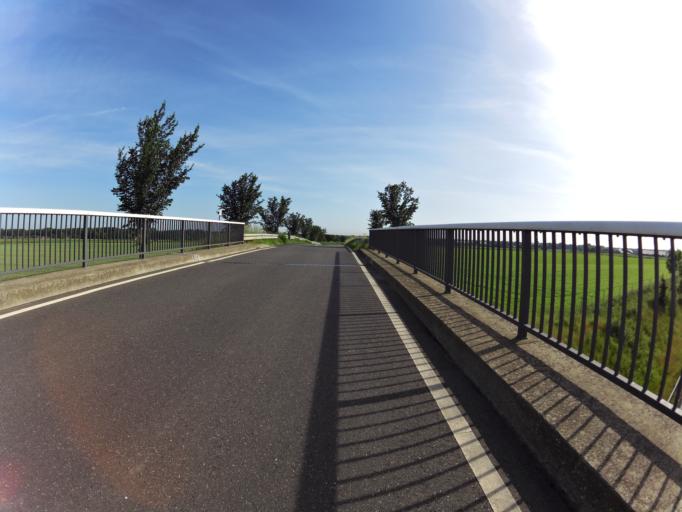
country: DE
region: North Rhine-Westphalia
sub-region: Regierungsbezirk Koln
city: Gangelt
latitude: 51.0157
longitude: 5.9851
